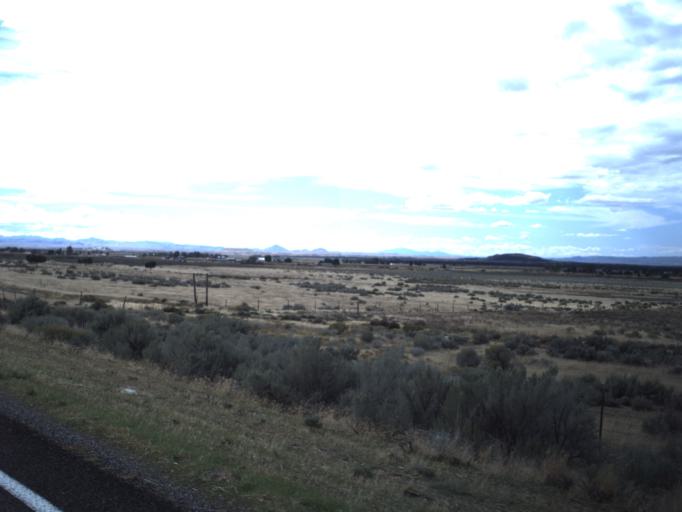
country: US
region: Utah
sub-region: Millard County
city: Fillmore
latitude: 39.0019
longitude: -112.4126
